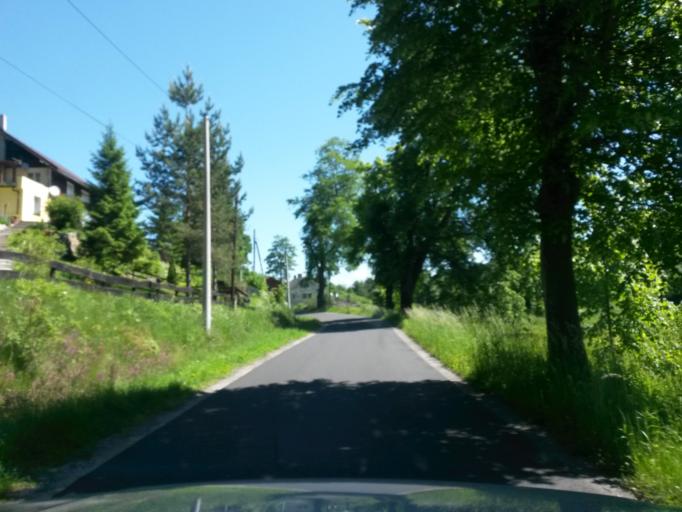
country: PL
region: Lower Silesian Voivodeship
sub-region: Powiat jeleniogorski
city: Podgorzyn
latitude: 50.8242
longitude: 15.6595
